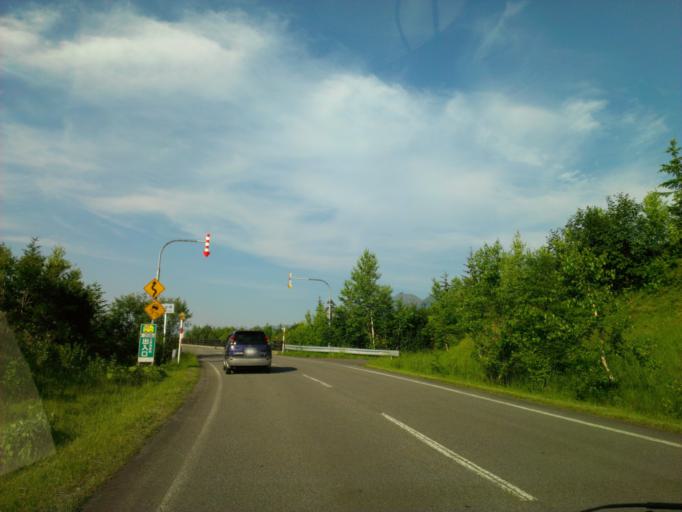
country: JP
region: Hokkaido
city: Shimo-furano
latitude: 43.4596
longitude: 142.6436
